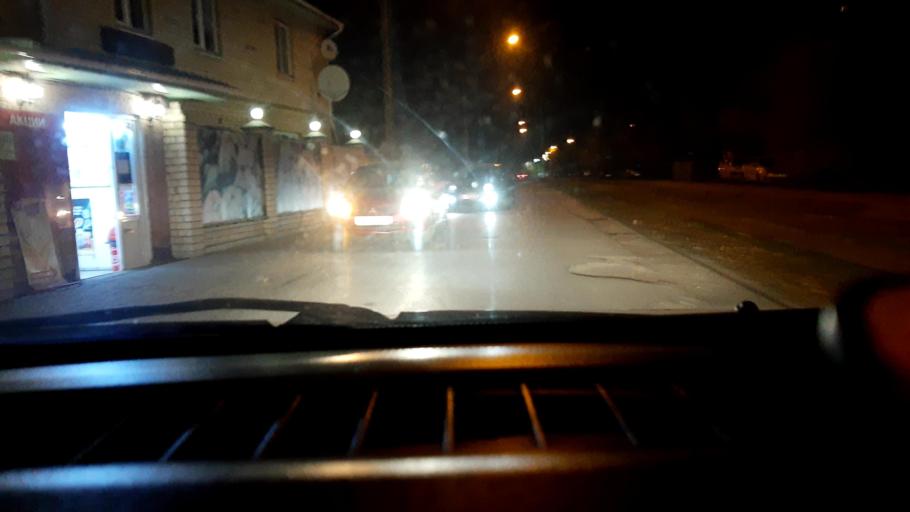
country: RU
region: Nizjnij Novgorod
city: Nizhniy Novgorod
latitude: 56.3075
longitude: 43.9210
